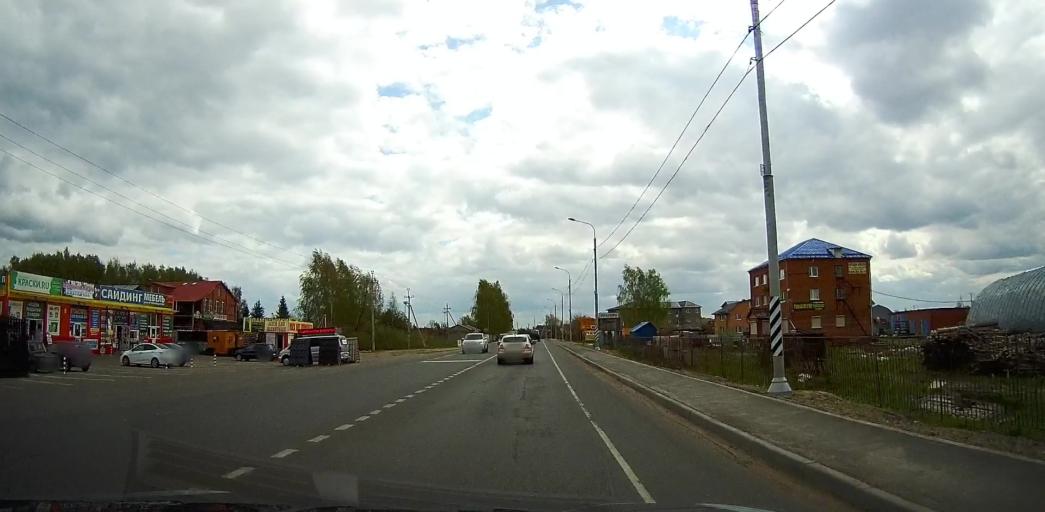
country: RU
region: Moskovskaya
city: Beloozerskiy
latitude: 55.4513
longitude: 38.4384
